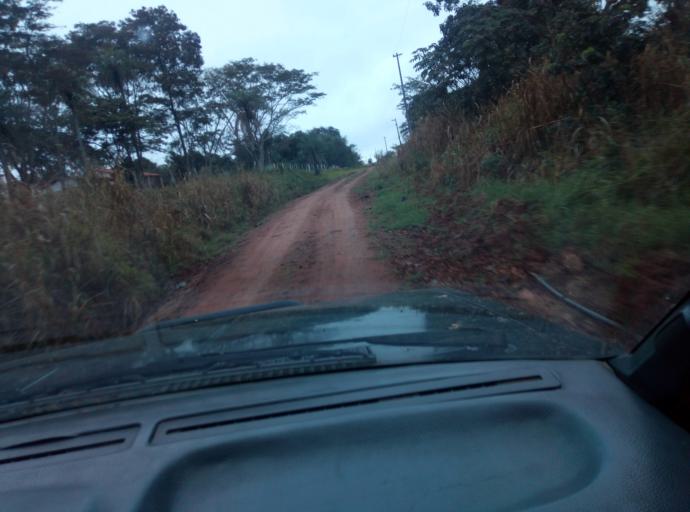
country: PY
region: Caaguazu
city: Carayao
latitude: -25.1904
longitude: -56.3533
